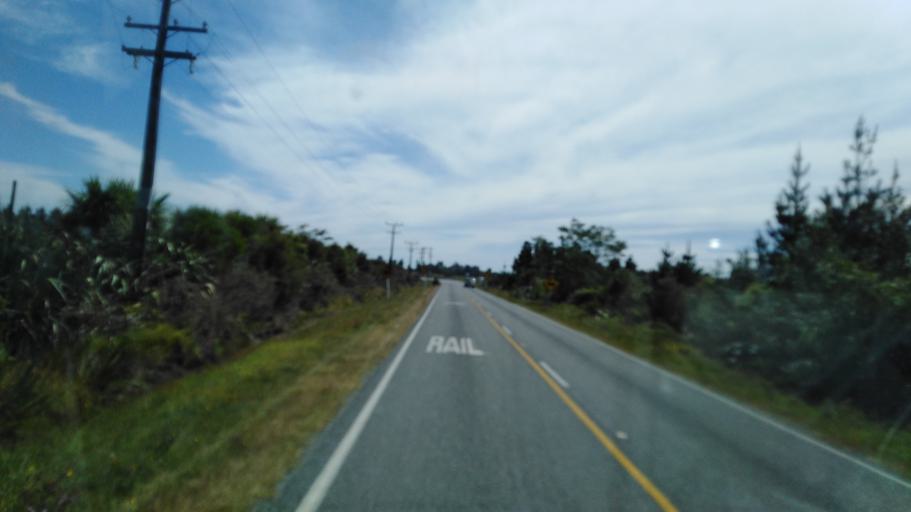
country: NZ
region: West Coast
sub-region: Buller District
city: Westport
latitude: -41.7387
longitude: 171.7075
